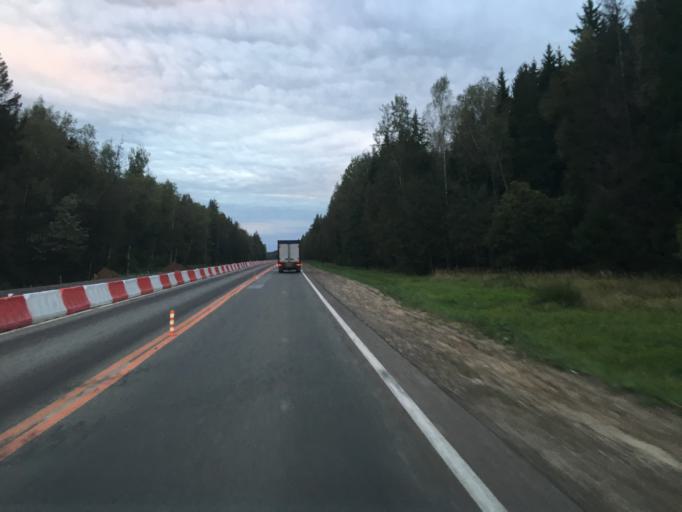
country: RU
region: Kaluga
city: Detchino
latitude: 54.6911
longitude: 36.2962
